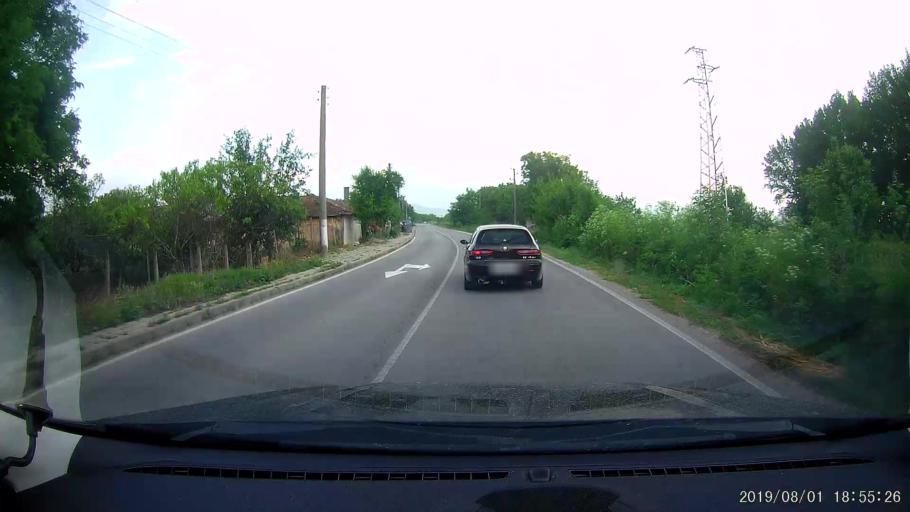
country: BG
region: Shumen
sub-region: Obshtina Smyadovo
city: Smyadovo
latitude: 43.1812
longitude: 27.0058
